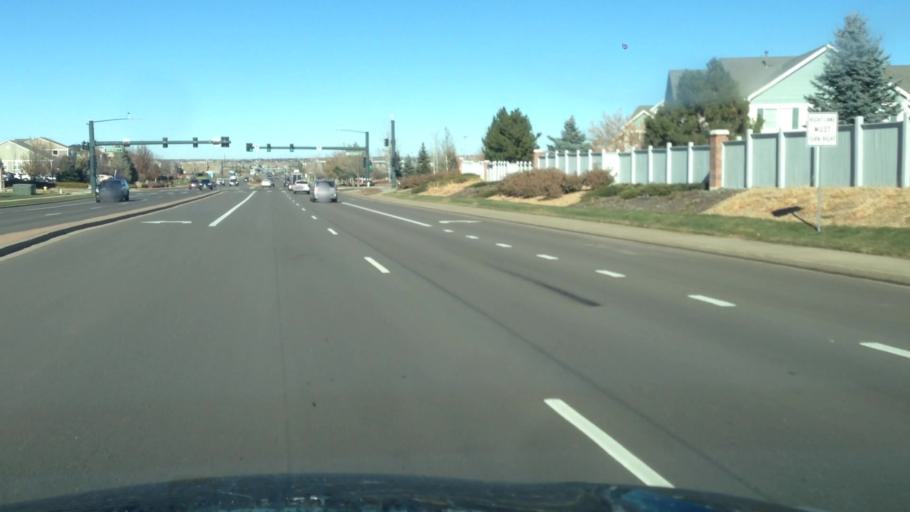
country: US
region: Colorado
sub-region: Douglas County
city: Stonegate
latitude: 39.5385
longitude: -104.7934
